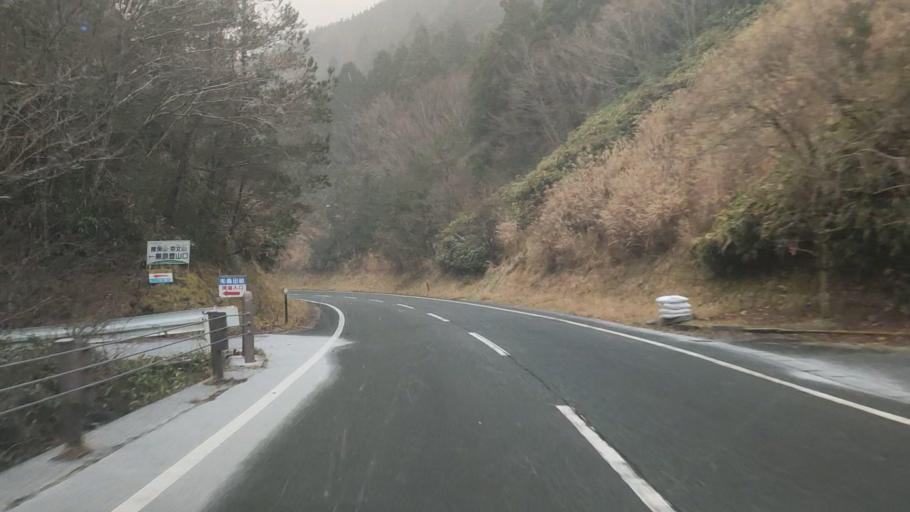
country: JP
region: Kumamoto
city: Matsubase
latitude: 32.5678
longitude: 130.9095
